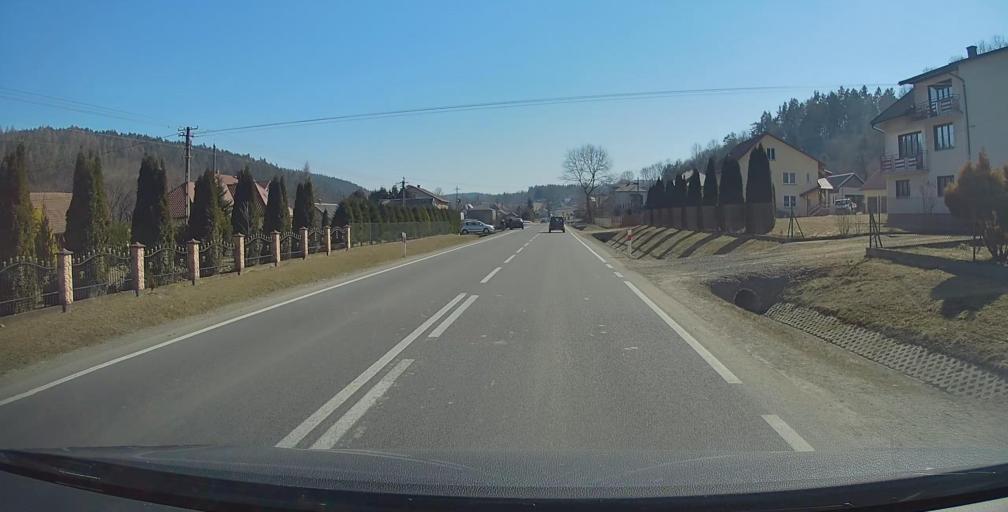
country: PL
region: Subcarpathian Voivodeship
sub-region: Powiat przemyski
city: Bircza
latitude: 49.6674
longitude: 22.4309
